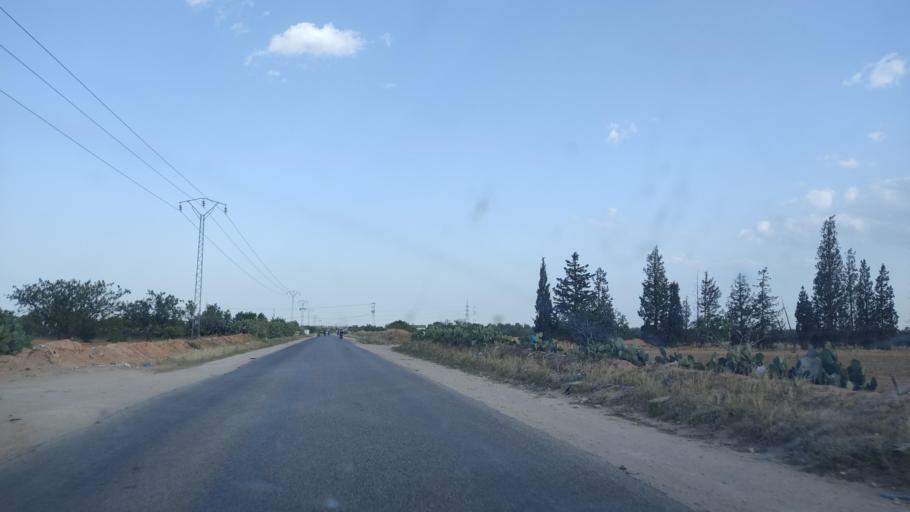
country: TN
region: Safaqis
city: Sfax
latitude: 34.8384
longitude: 10.6266
